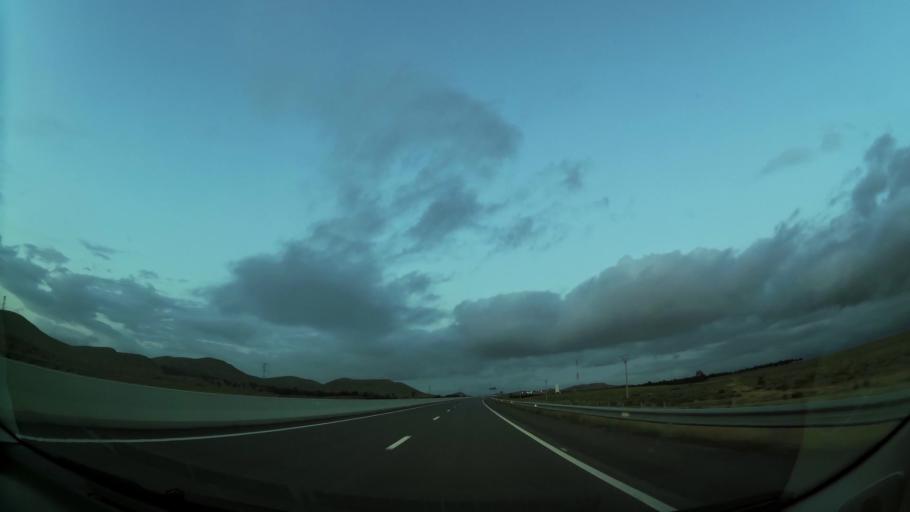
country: MA
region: Oriental
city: El Aioun
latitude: 34.6173
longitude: -2.4489
